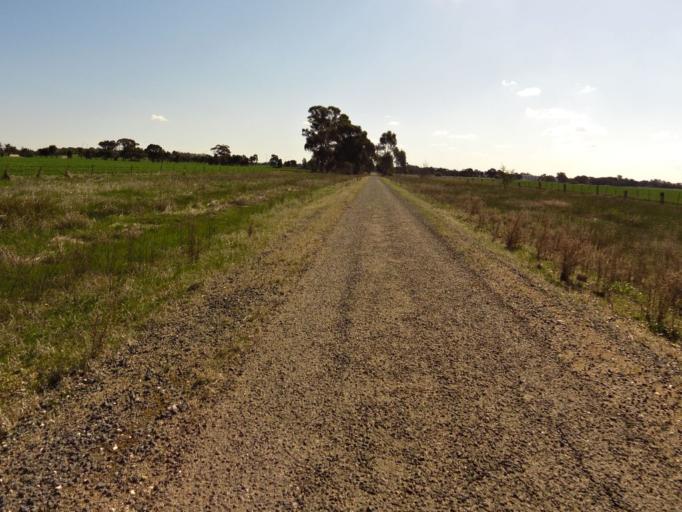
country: AU
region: New South Wales
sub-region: Corowa Shire
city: Corowa
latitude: -36.0188
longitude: 146.4191
